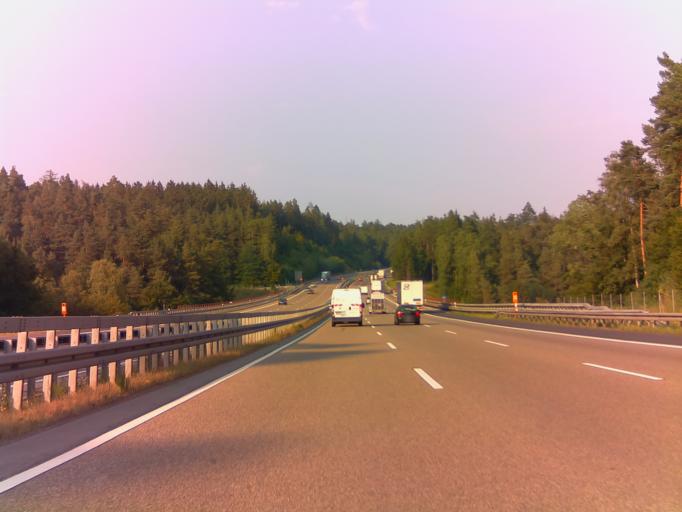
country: DE
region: Hesse
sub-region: Regierungsbezirk Kassel
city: Niederaula
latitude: 50.8431
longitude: 9.6236
